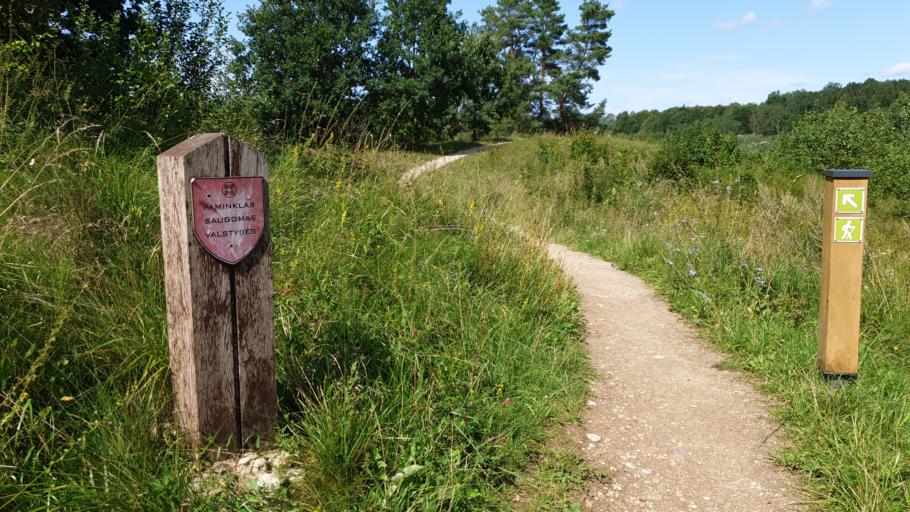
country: LT
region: Vilnius County
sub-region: Vilniaus Rajonas
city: Vievis
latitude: 54.8239
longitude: 24.9447
